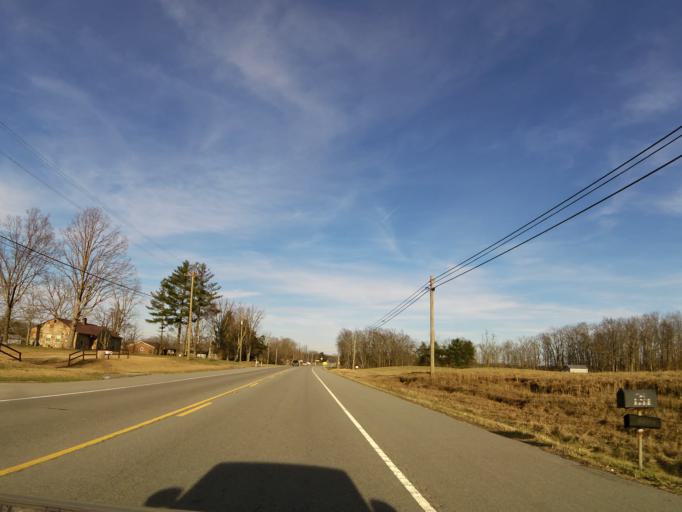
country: US
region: Tennessee
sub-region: White County
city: Sparta
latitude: 35.9403
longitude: -85.3368
